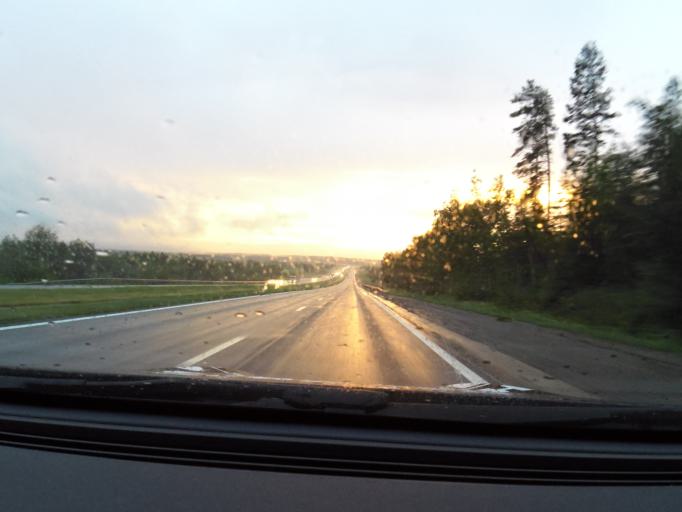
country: RU
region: Tatarstan
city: Mendeleyevsk
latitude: 55.7597
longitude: 52.2319
